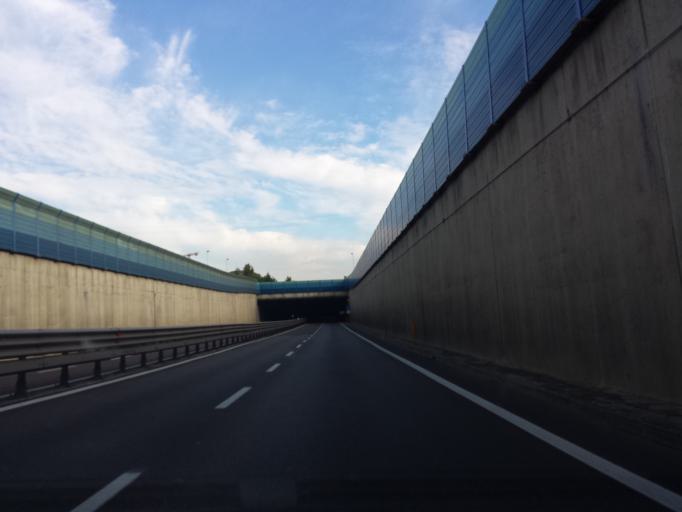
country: IT
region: Veneto
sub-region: Provincia di Verona
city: San Giovanni Lupatoto
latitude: 45.3814
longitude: 11.0334
